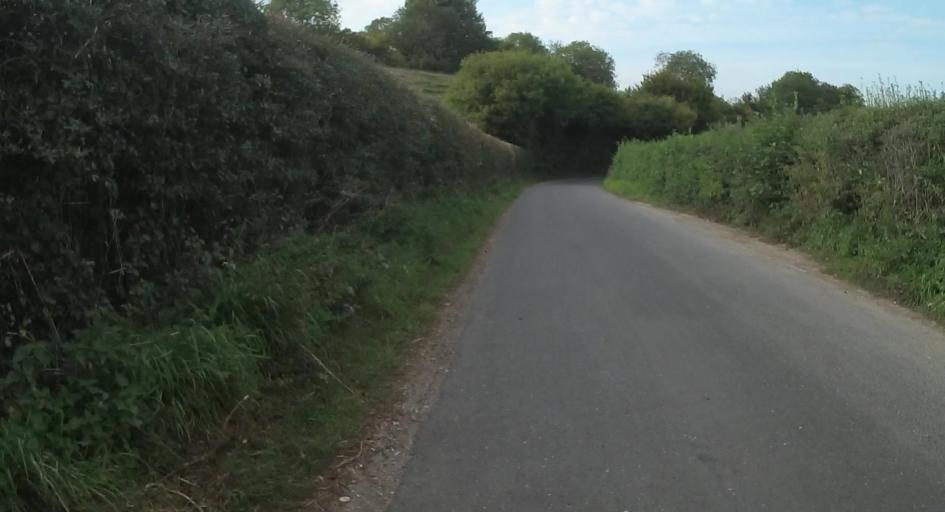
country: GB
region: England
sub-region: Hampshire
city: Kings Worthy
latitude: 51.0646
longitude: -1.1815
